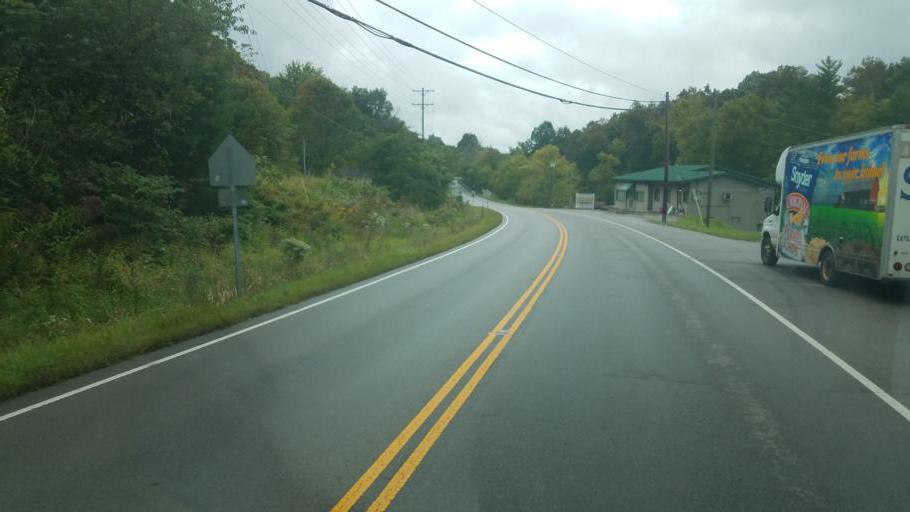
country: US
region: Ohio
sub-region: Scioto County
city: Sciotodale
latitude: 38.8164
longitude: -82.7388
